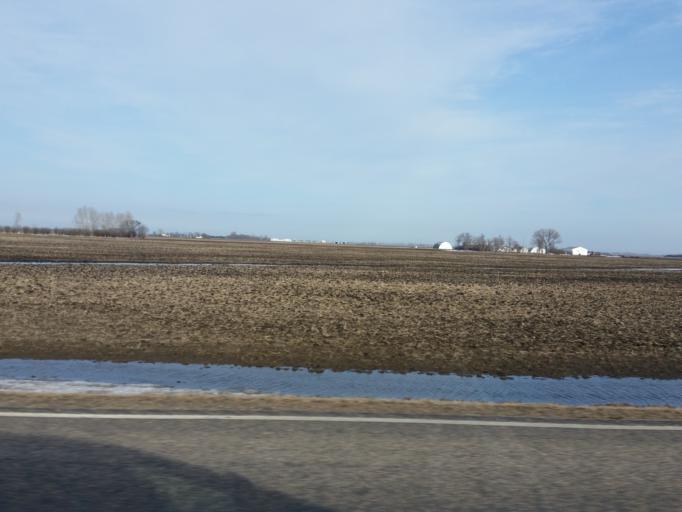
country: US
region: North Dakota
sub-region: Walsh County
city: Grafton
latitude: 48.4240
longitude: -97.2996
